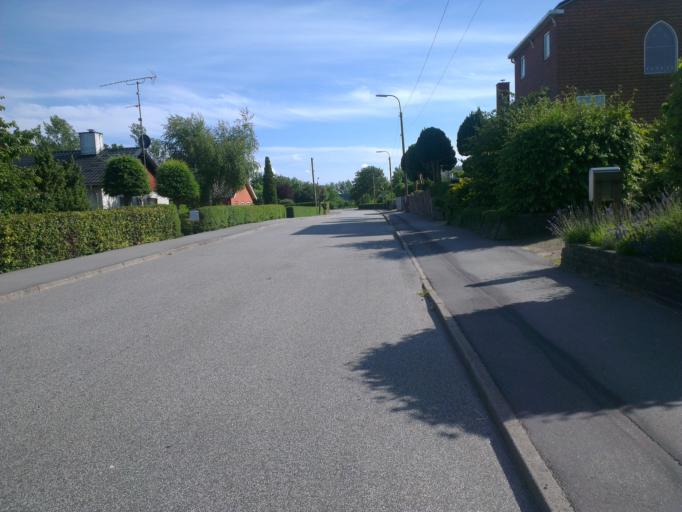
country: DK
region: Capital Region
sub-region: Frederikssund Kommune
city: Skibby
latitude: 55.7495
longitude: 11.9657
